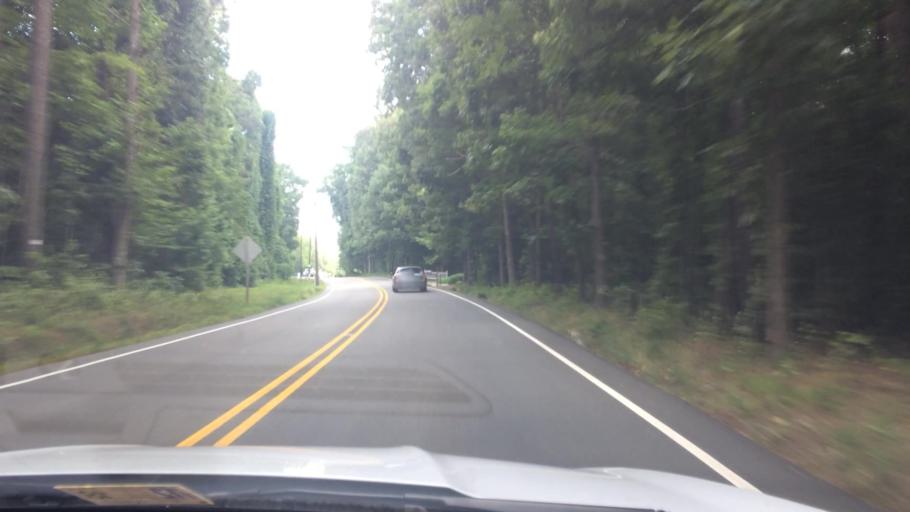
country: US
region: Virginia
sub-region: King William County
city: West Point
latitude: 37.6049
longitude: -76.7723
